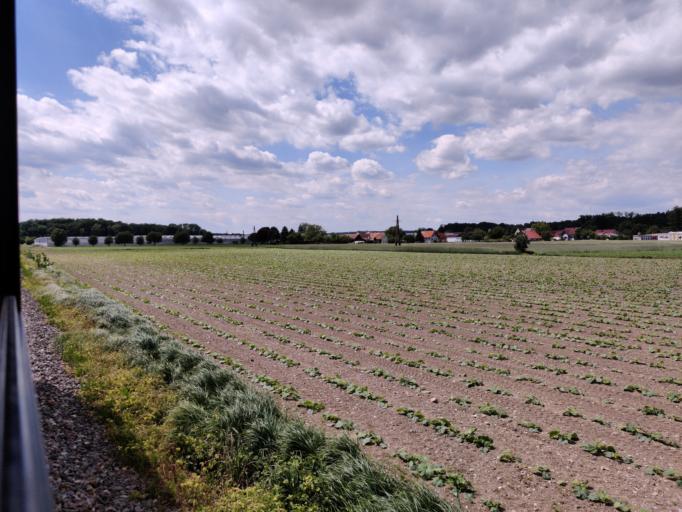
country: AT
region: Styria
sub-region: Politischer Bezirk Suedoststeiermark
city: Deutsch Goritz
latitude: 46.7324
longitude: 15.8755
